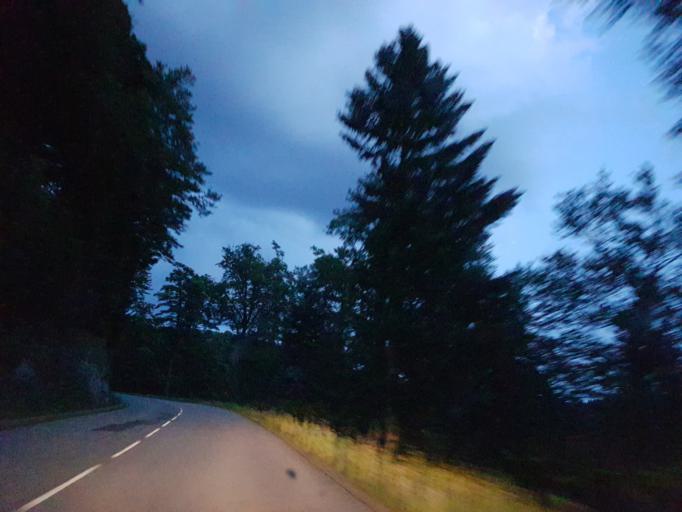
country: FR
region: Lorraine
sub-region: Departement des Vosges
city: Xonrupt-Longemer
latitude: 48.0538
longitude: 6.9980
